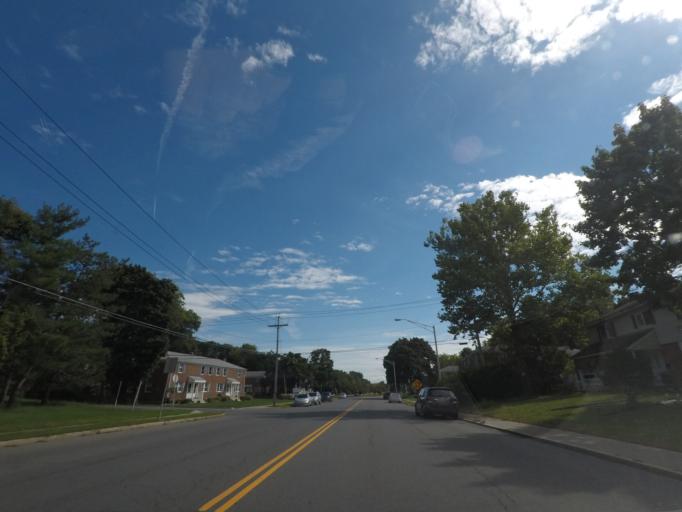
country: US
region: New York
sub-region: Albany County
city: West Albany
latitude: 42.6530
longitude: -73.8045
